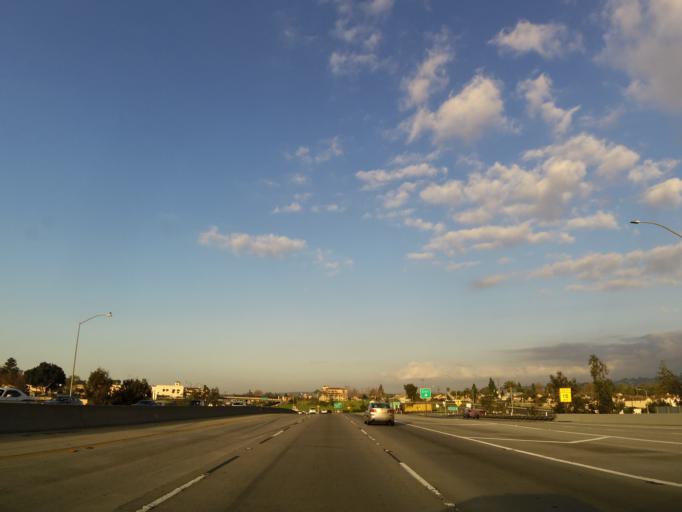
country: US
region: California
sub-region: Ventura County
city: Camarillo
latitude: 34.2168
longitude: -119.0336
